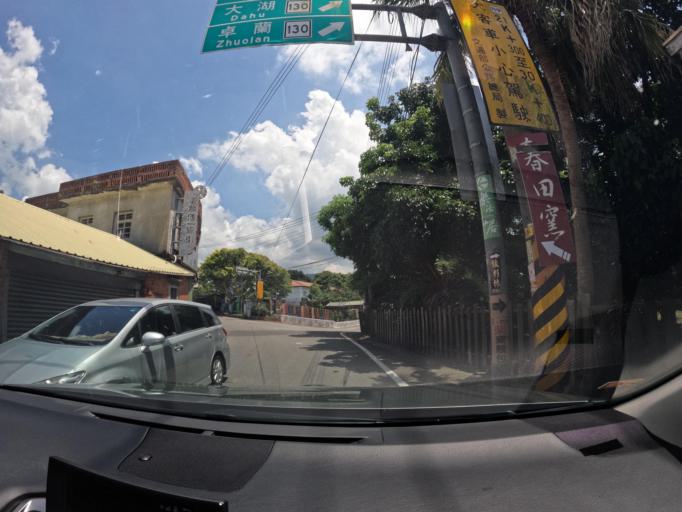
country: TW
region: Taiwan
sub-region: Miaoli
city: Miaoli
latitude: 24.4104
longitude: 120.7808
